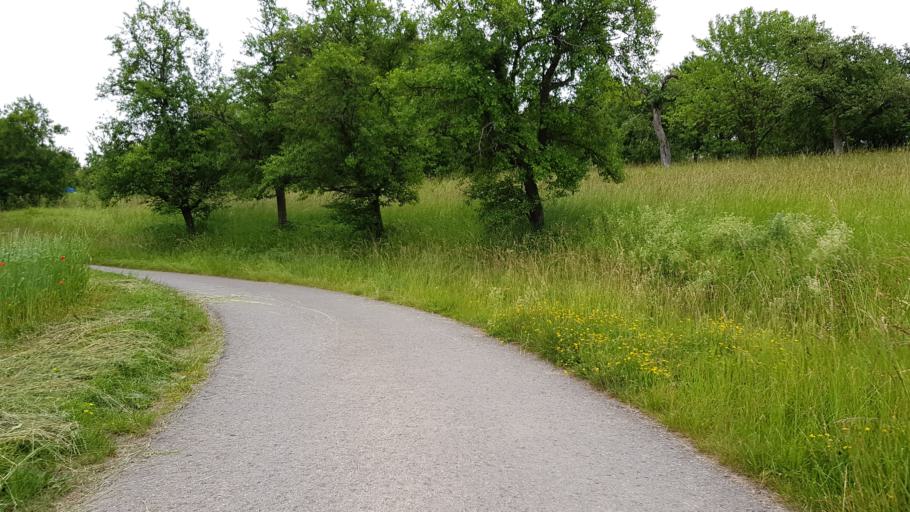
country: DE
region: Baden-Wuerttemberg
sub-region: Regierungsbezirk Stuttgart
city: Steinheim am der Murr
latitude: 48.9598
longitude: 9.2756
